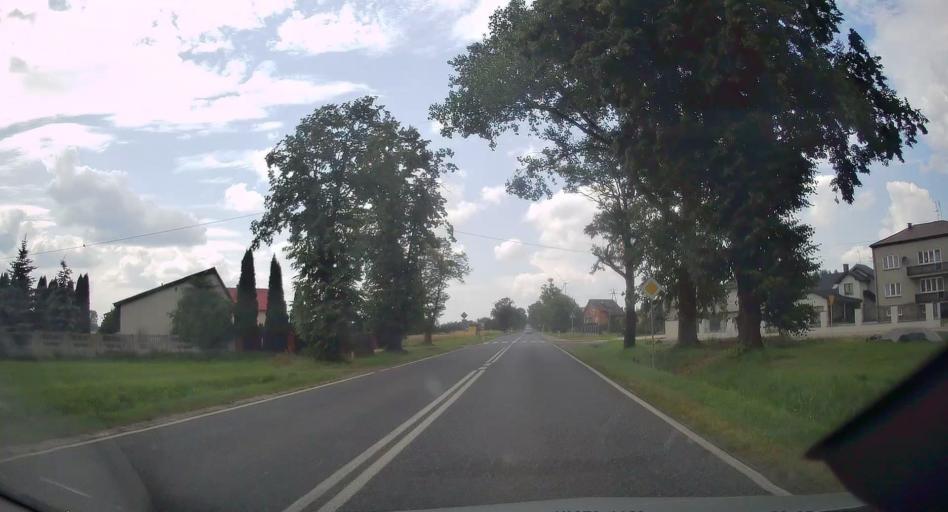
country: PL
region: Lodz Voivodeship
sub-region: Powiat skierniewicki
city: Gluchow
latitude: 51.7798
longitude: 20.0641
